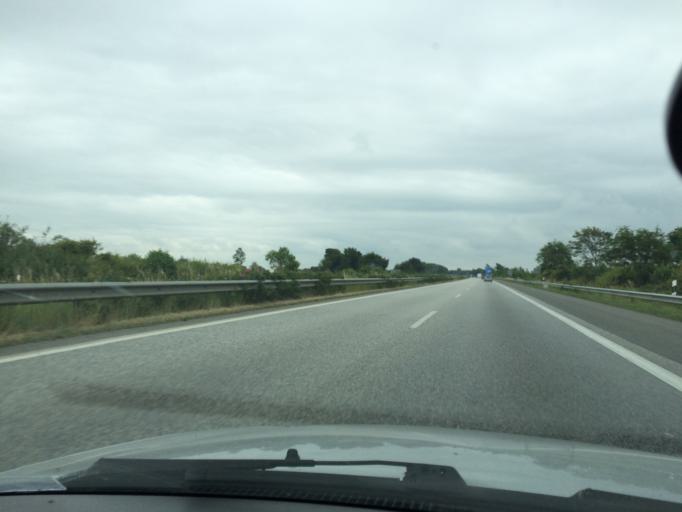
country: DE
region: Schleswig-Holstein
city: Handewitt
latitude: 54.7830
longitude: 9.3397
